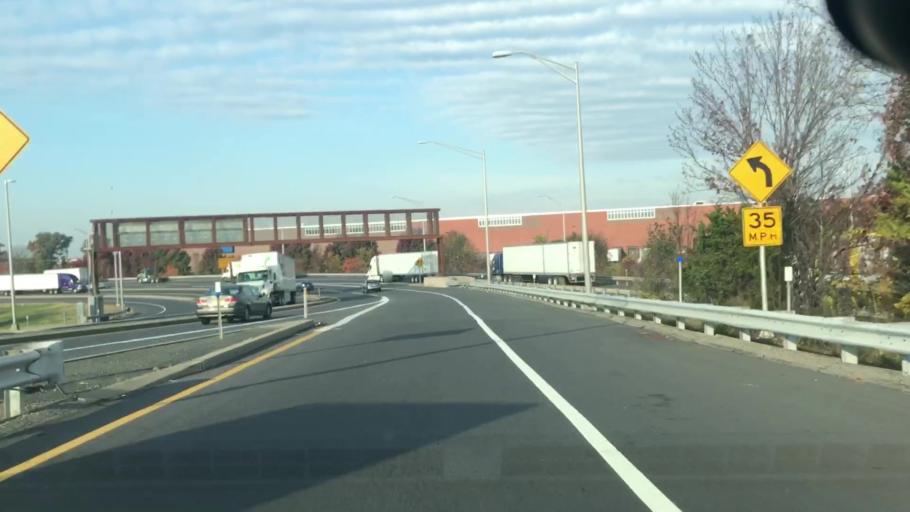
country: US
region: New Jersey
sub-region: Middlesex County
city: Rossmoor
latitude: 40.3519
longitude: -74.4752
